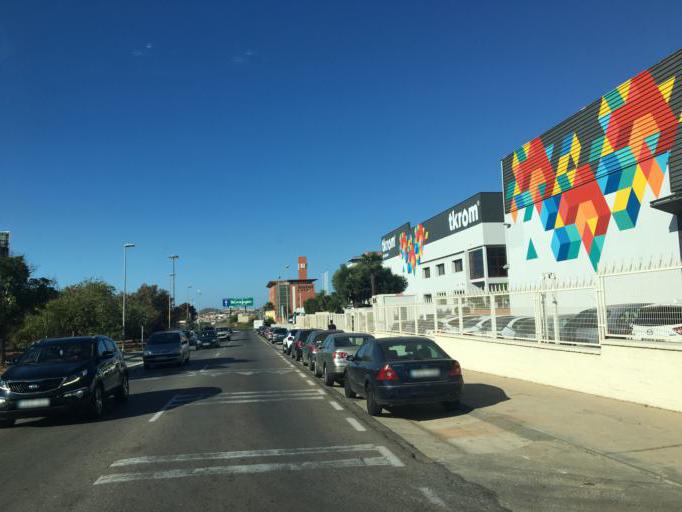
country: ES
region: Murcia
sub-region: Murcia
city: Cartagena
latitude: 37.6188
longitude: -0.9533
